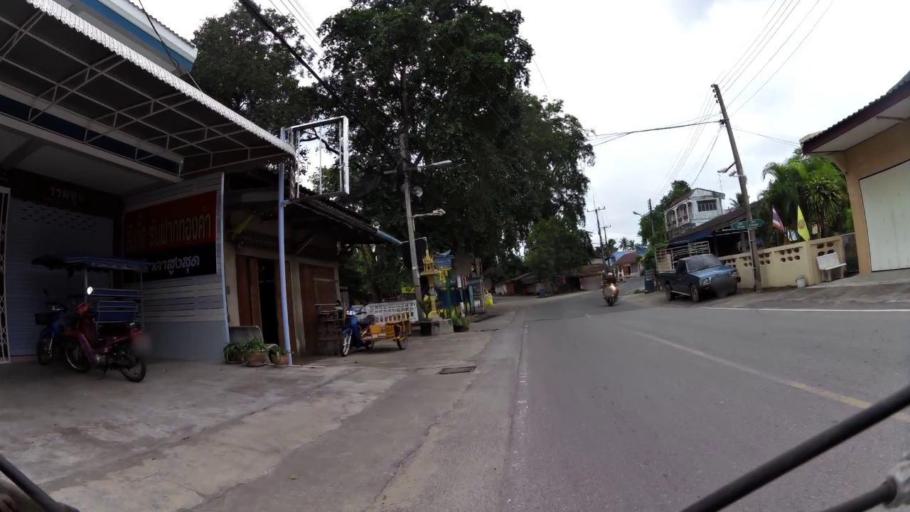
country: TH
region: Prachuap Khiri Khan
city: Prachuap Khiri Khan
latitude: 11.7477
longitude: 99.7901
